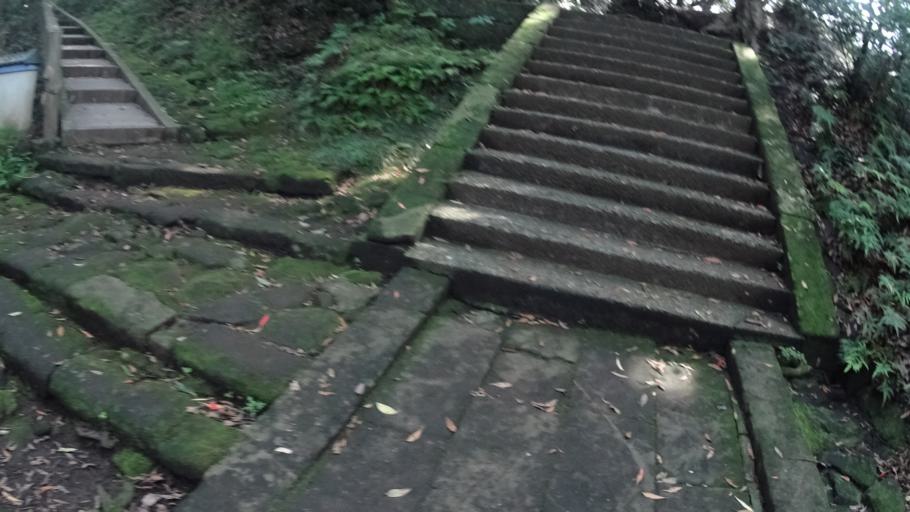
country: JP
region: Kanagawa
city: Zushi
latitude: 35.3037
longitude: 139.6064
